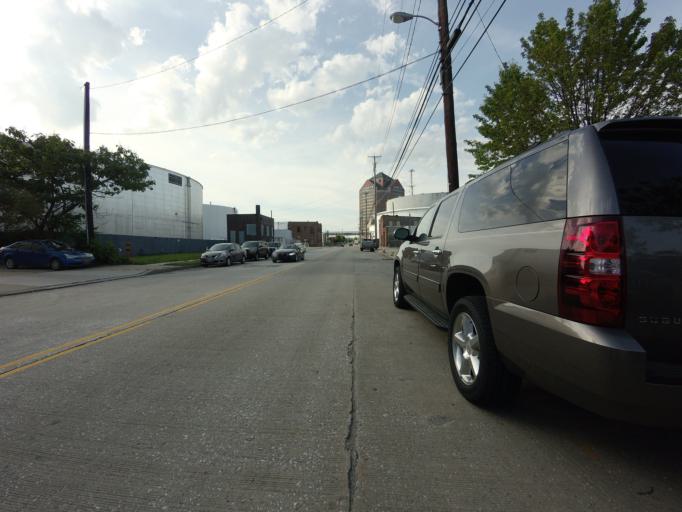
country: US
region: Maryland
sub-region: City of Baltimore
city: Baltimore
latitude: 39.2722
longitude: -76.5690
